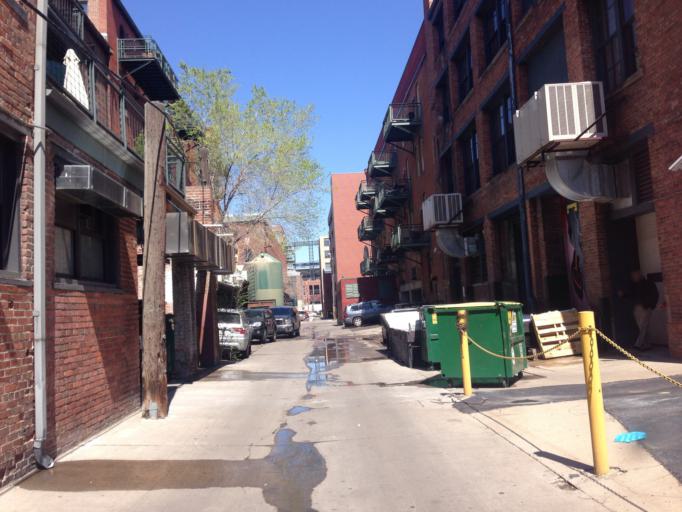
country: US
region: Colorado
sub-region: Denver County
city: Denver
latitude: 39.7529
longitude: -104.9988
